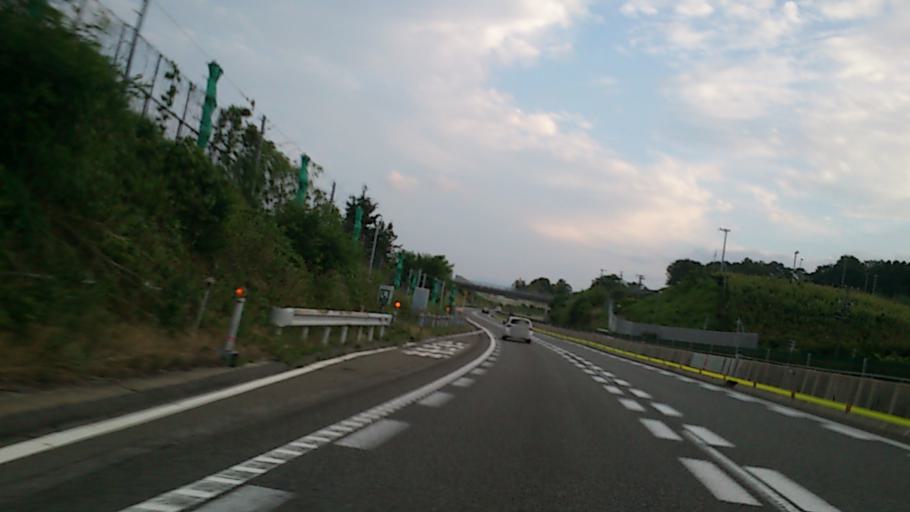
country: JP
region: Nagano
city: Iida
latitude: 35.5685
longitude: 137.8714
